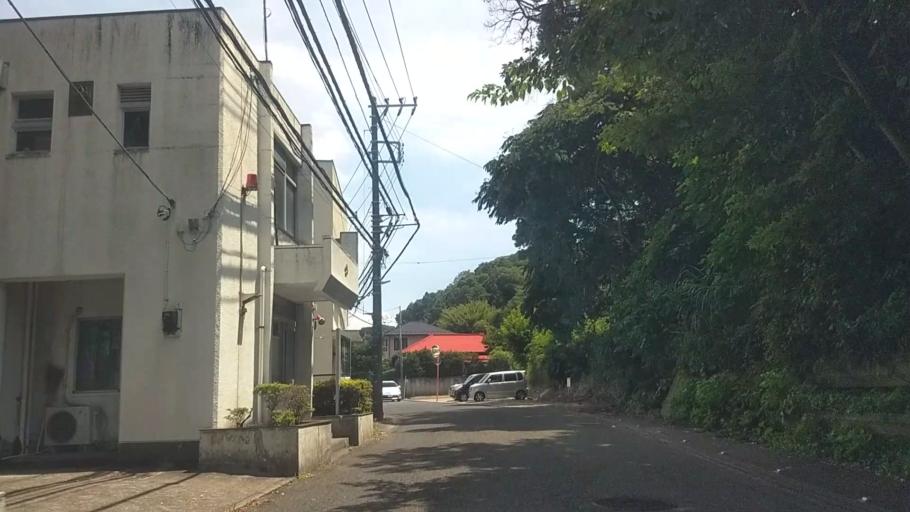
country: JP
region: Kanagawa
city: Kamakura
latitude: 35.3002
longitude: 139.5610
